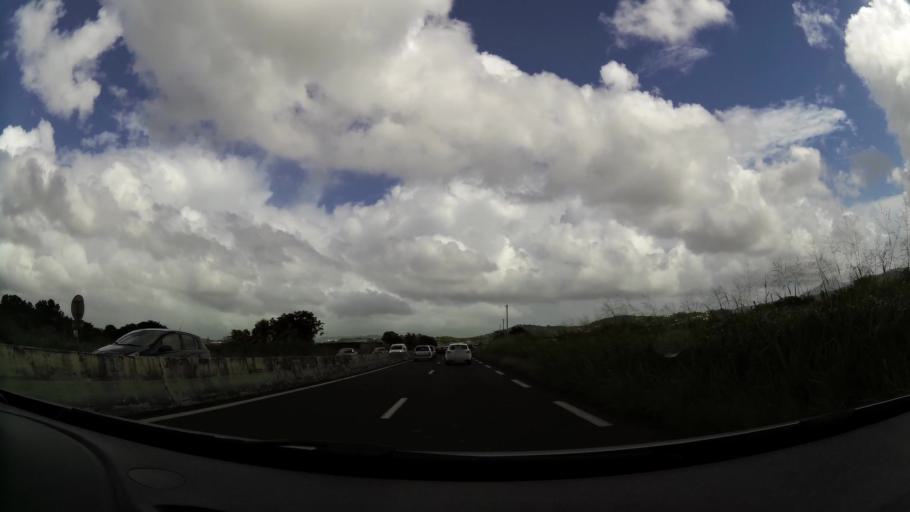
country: MQ
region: Martinique
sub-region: Martinique
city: Ducos
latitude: 14.5413
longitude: -60.9774
